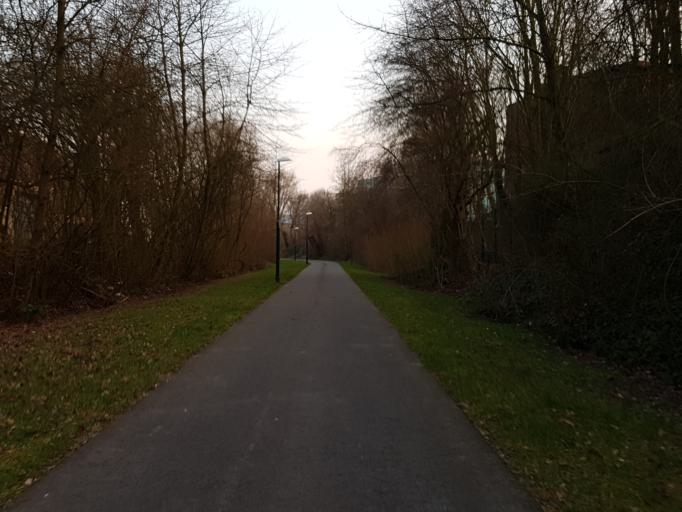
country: DE
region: North Rhine-Westphalia
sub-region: Regierungsbezirk Koln
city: Aachen
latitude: 50.7925
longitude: 6.1038
